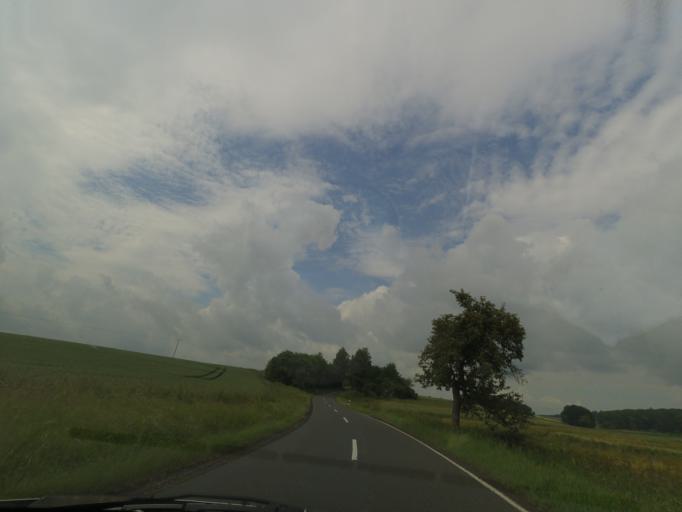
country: DE
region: Hesse
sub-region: Regierungsbezirk Giessen
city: Fronhausen
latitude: 50.7344
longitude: 8.6818
